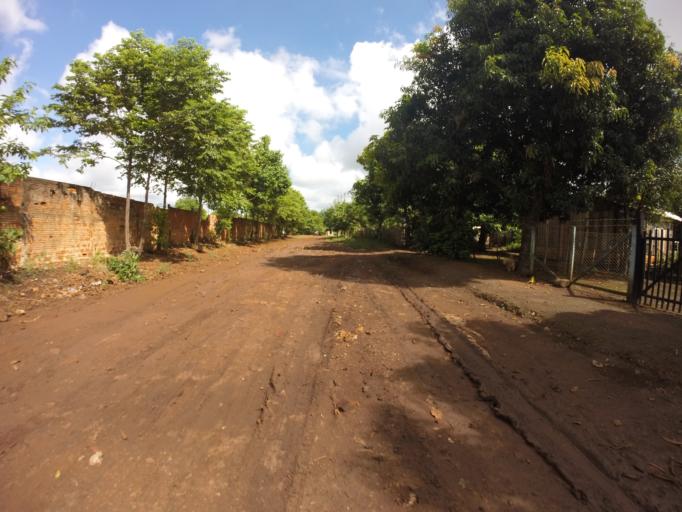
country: PY
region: Alto Parana
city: Ciudad del Este
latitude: -25.3969
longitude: -54.6491
